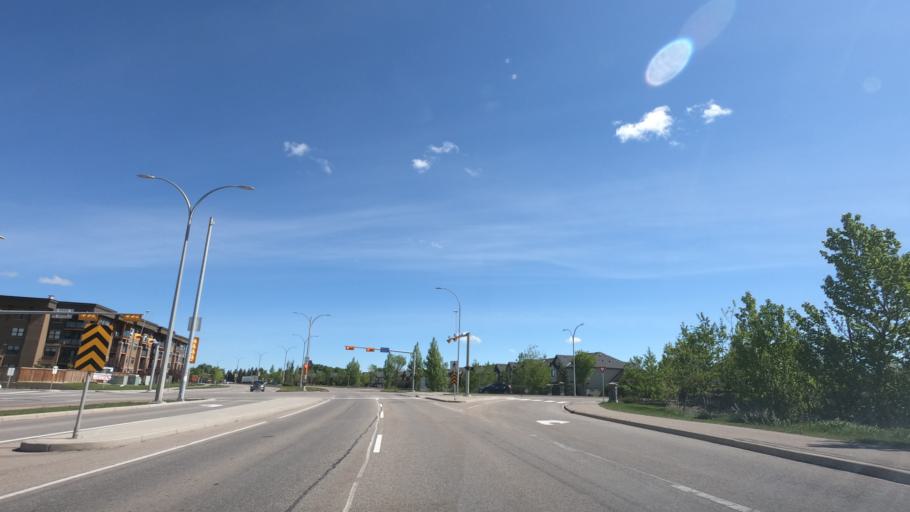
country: CA
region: Alberta
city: Airdrie
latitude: 51.2676
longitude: -113.9907
